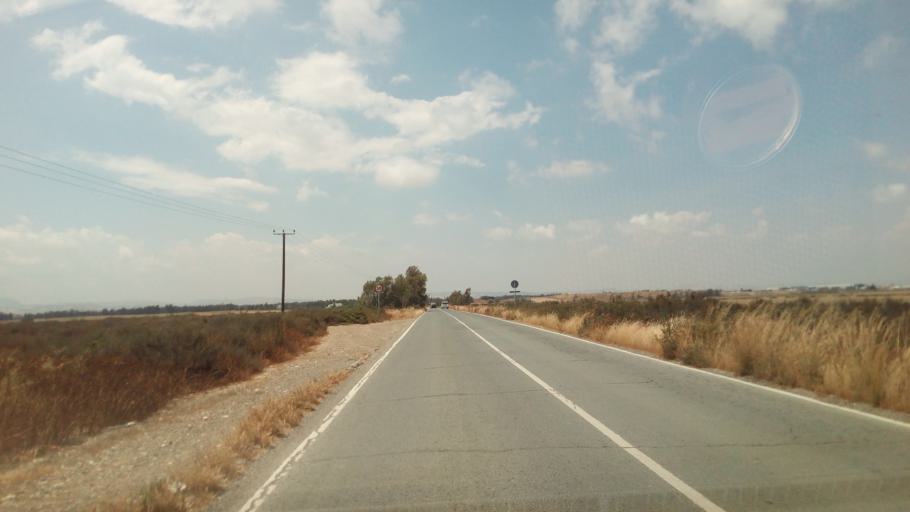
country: CY
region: Larnaka
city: Meneou
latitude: 34.8464
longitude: 33.6154
